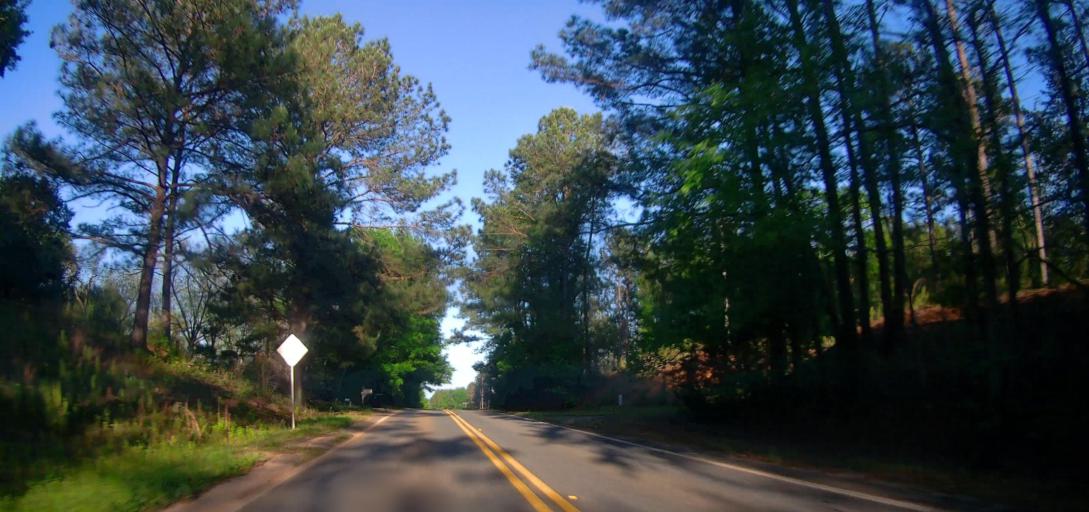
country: US
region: Georgia
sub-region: Schley County
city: Ellaville
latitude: 32.3221
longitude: -84.2364
